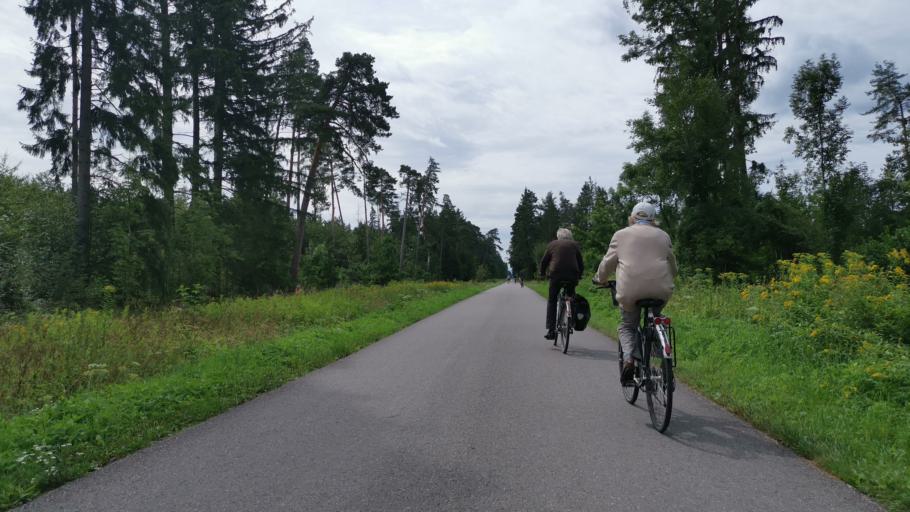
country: DE
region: Bavaria
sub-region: Upper Bavaria
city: Unterhaching
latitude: 48.0798
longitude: 11.5736
